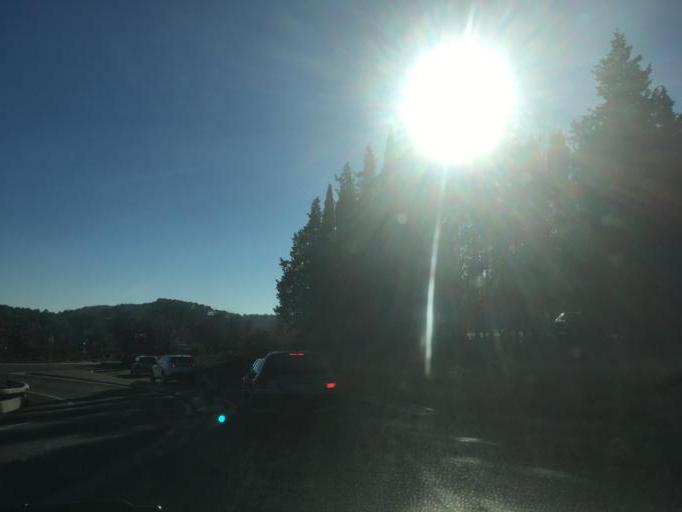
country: FR
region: Provence-Alpes-Cote d'Azur
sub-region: Departement du Var
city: Flayosc
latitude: 43.5341
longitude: 6.4042
